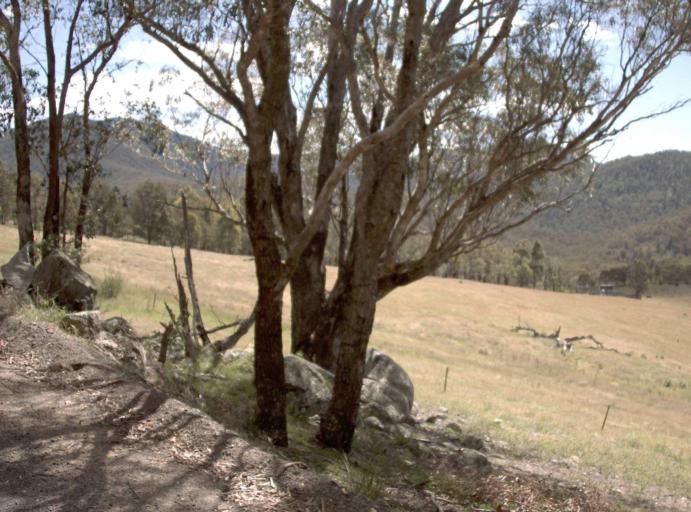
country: AU
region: New South Wales
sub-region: Bombala
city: Bombala
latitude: -37.1460
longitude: 148.6620
